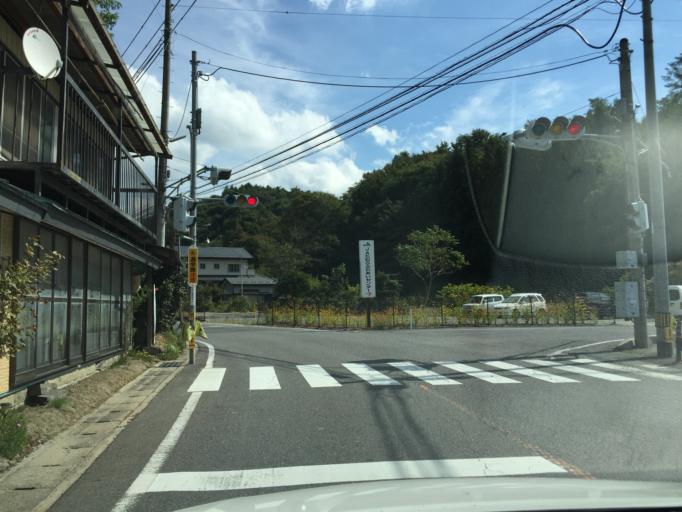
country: JP
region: Fukushima
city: Funehikimachi-funehiki
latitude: 37.4107
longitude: 140.5415
